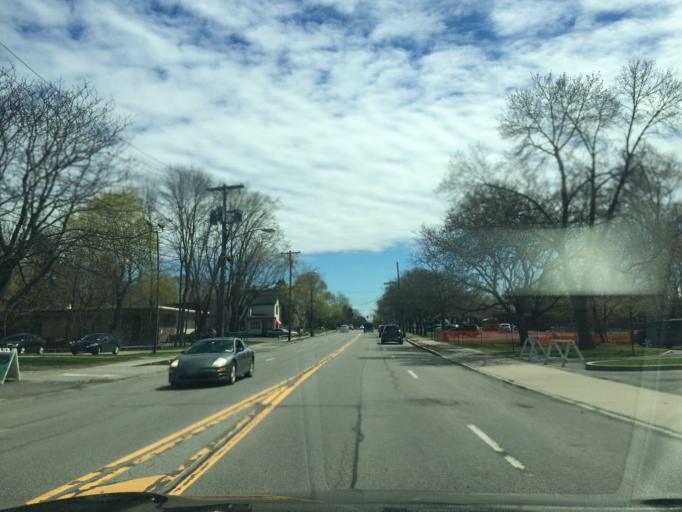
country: US
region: New York
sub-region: Monroe County
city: Brighton
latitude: 43.1258
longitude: -77.5639
